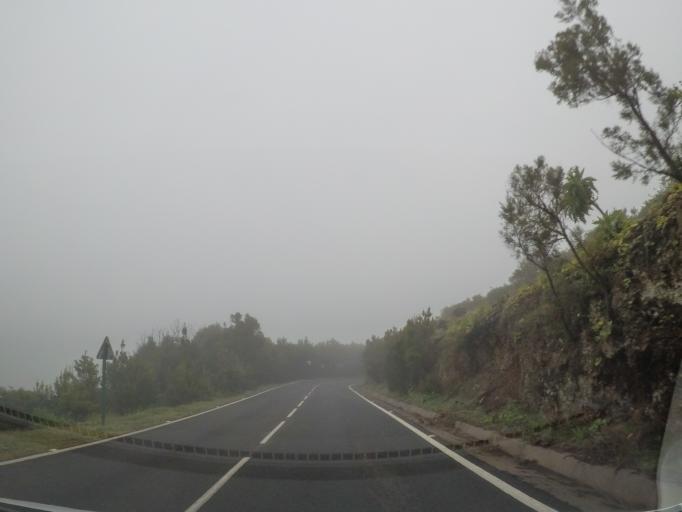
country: ES
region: Canary Islands
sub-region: Provincia de Santa Cruz de Tenerife
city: Alajero
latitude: 28.1070
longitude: -17.2428
